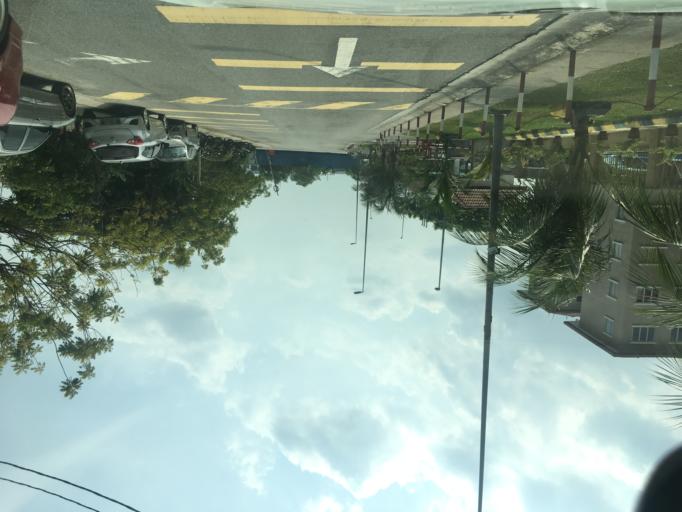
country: MY
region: Selangor
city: Shah Alam
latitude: 3.0813
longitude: 101.4795
